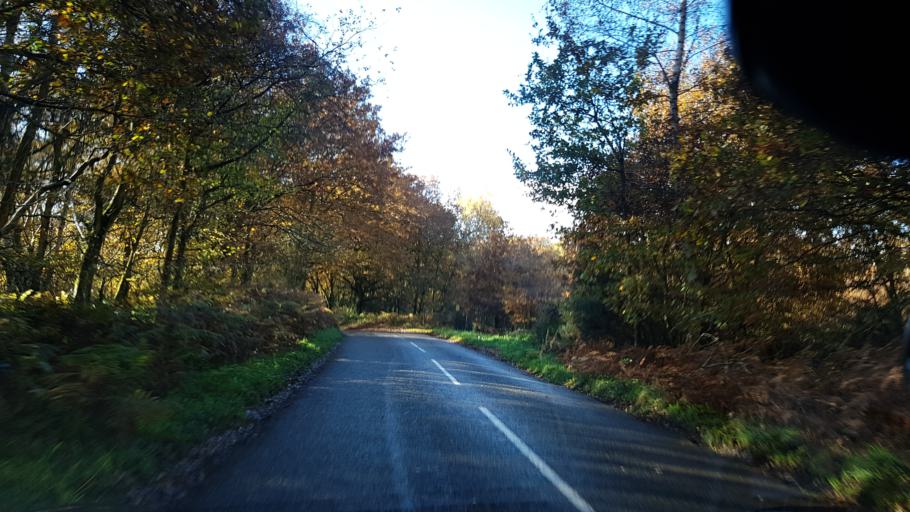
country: GB
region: England
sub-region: Surrey
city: Elstead
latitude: 51.2046
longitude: -0.6946
